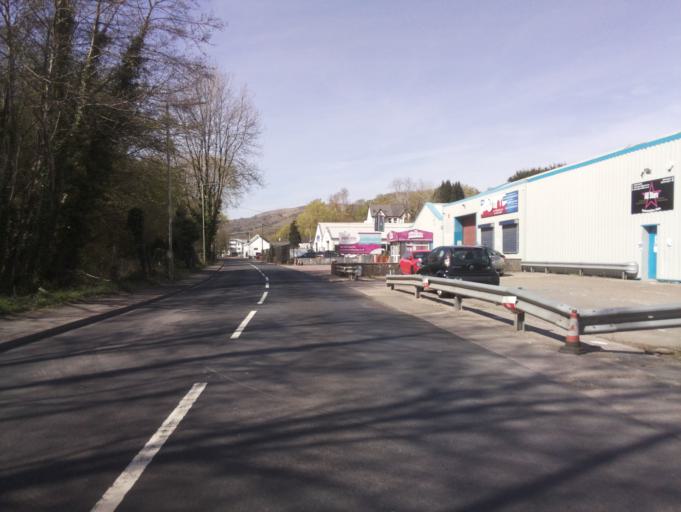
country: GB
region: Wales
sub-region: Caerphilly County Borough
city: Abertridwr
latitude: 51.5581
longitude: -3.2706
